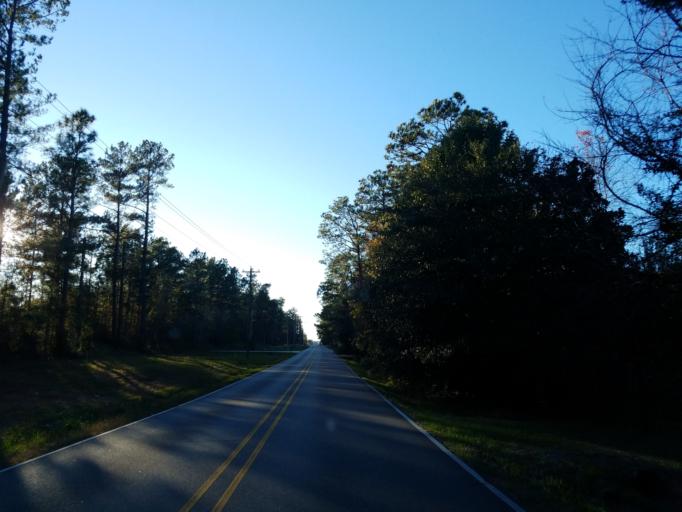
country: US
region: Mississippi
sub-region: Lamar County
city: Arnold Line
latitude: 31.3467
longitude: -89.3838
